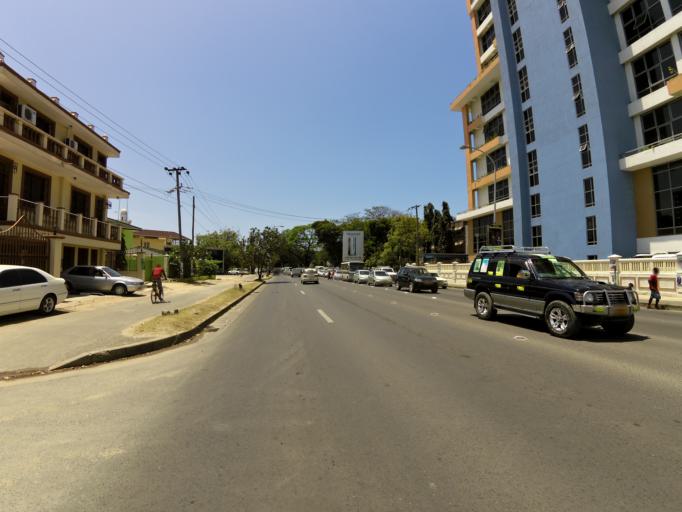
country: TZ
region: Dar es Salaam
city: Dar es Salaam
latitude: -6.8047
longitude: 39.2862
